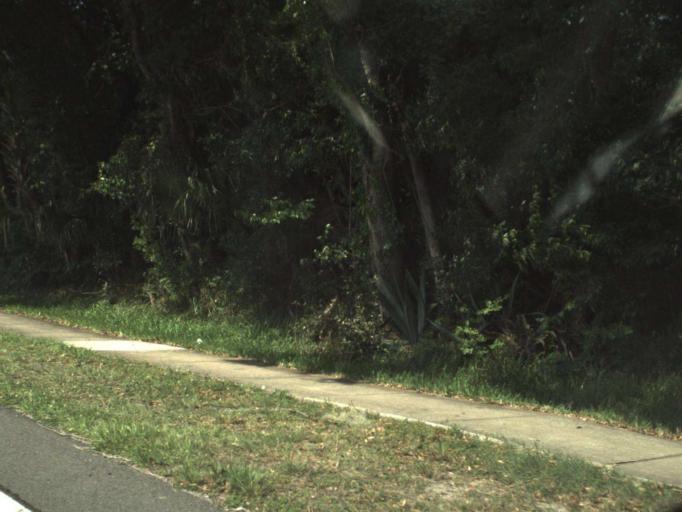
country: US
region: Florida
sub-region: Marion County
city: Belleview
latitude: 29.0681
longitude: -82.0695
